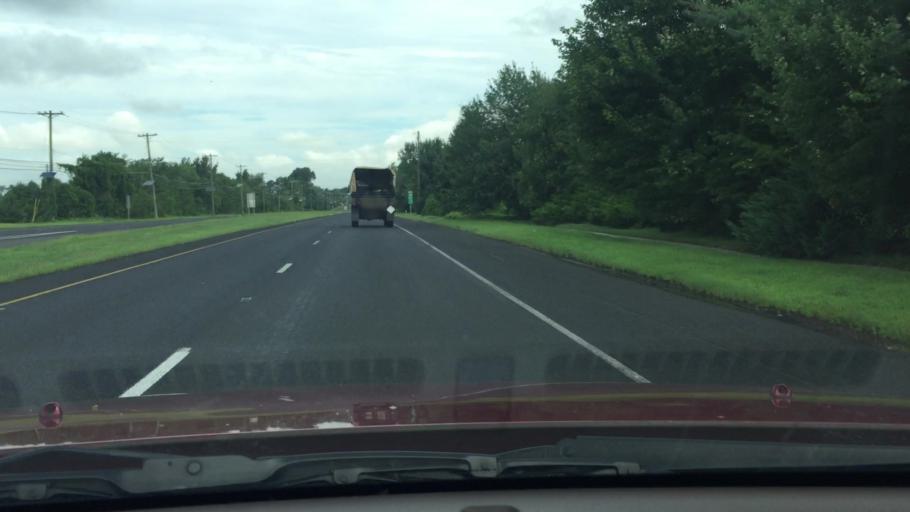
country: US
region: New Jersey
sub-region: Burlington County
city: Bordentown
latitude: 40.0876
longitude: -74.6746
